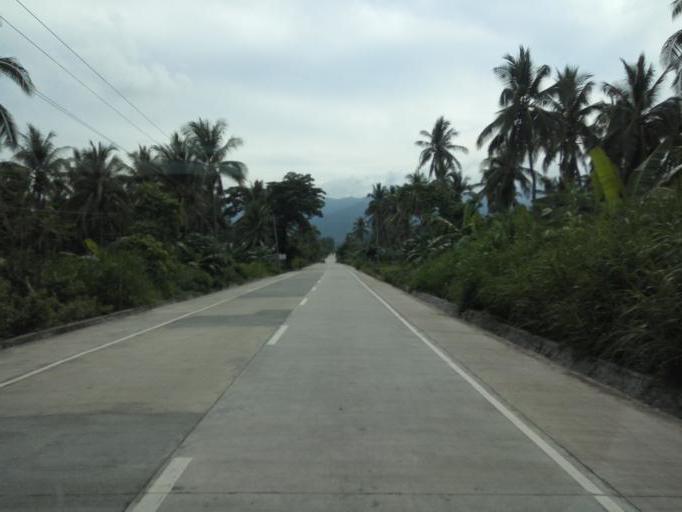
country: PH
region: Central Luzon
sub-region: Province of Aurora
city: Dinalongan
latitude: 16.0774
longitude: 121.7768
